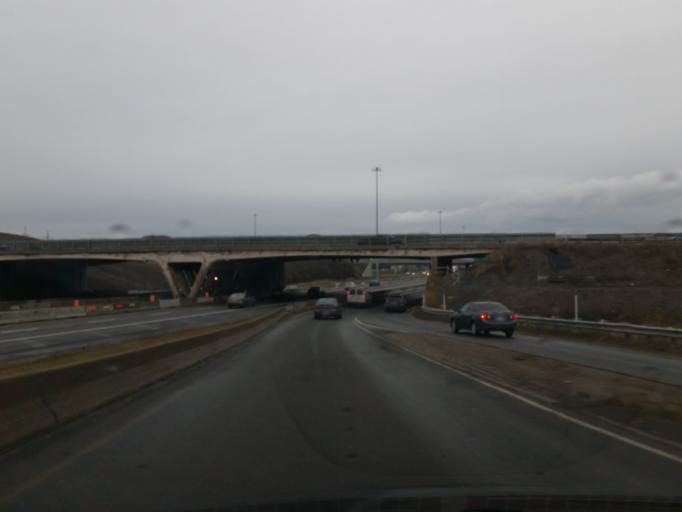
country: CA
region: Quebec
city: Quebec
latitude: 46.8366
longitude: -71.2630
